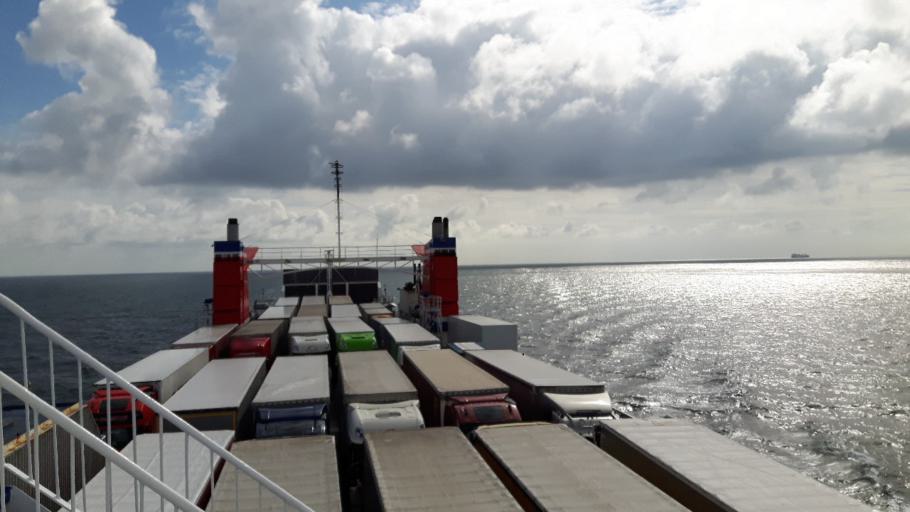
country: SE
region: Skane
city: Smygehamn
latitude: 54.9742
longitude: 13.6274
